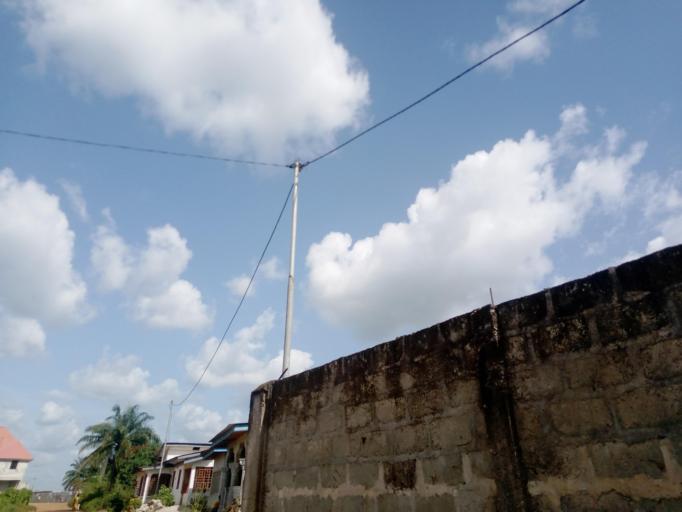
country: SL
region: Northern Province
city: Makeni
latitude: 8.9084
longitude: -12.0313
